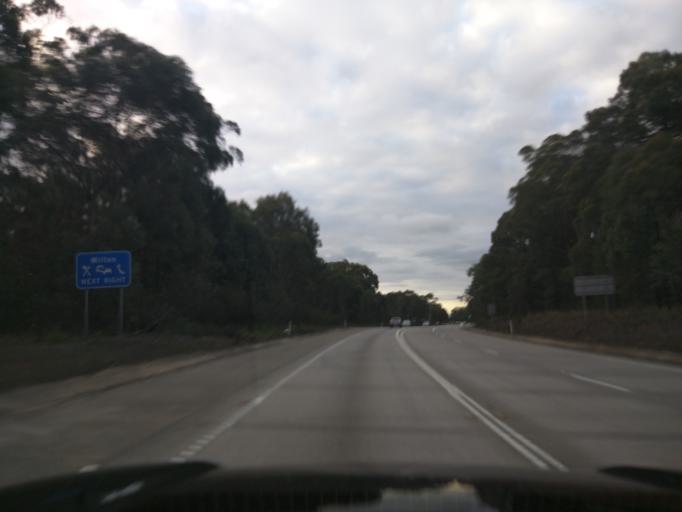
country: AU
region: New South Wales
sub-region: Wollondilly
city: Douglas Park
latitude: -34.2705
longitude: 150.7136
